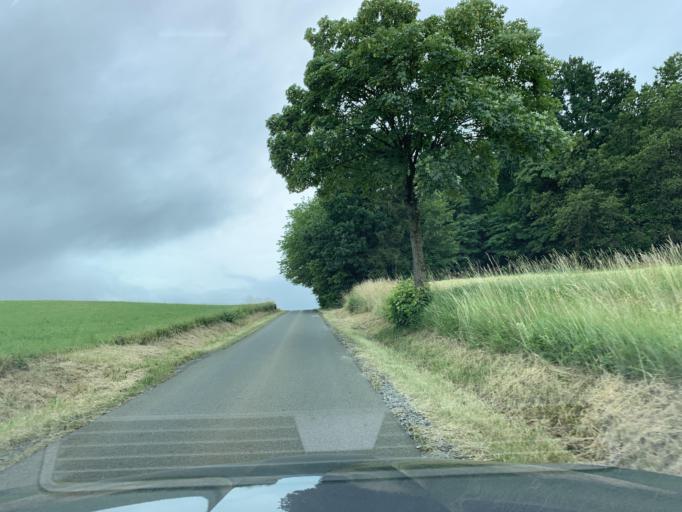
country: DE
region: Bavaria
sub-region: Upper Palatinate
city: Winklarn
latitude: 49.4264
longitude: 12.4700
